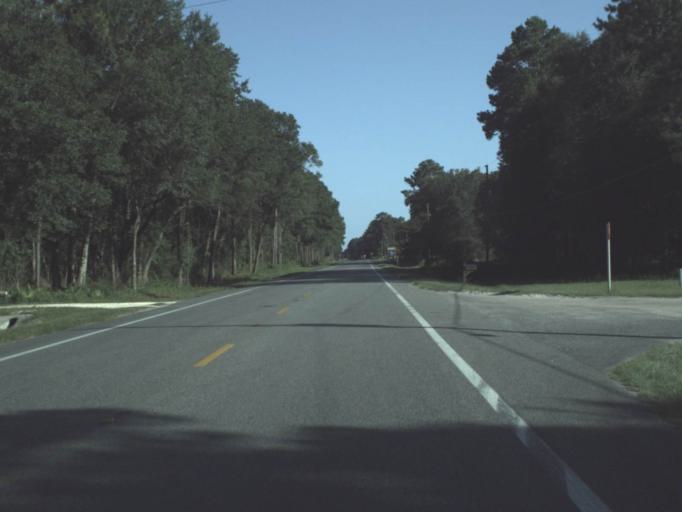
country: US
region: Florida
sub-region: Taylor County
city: Perry
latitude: 30.1697
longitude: -83.5969
